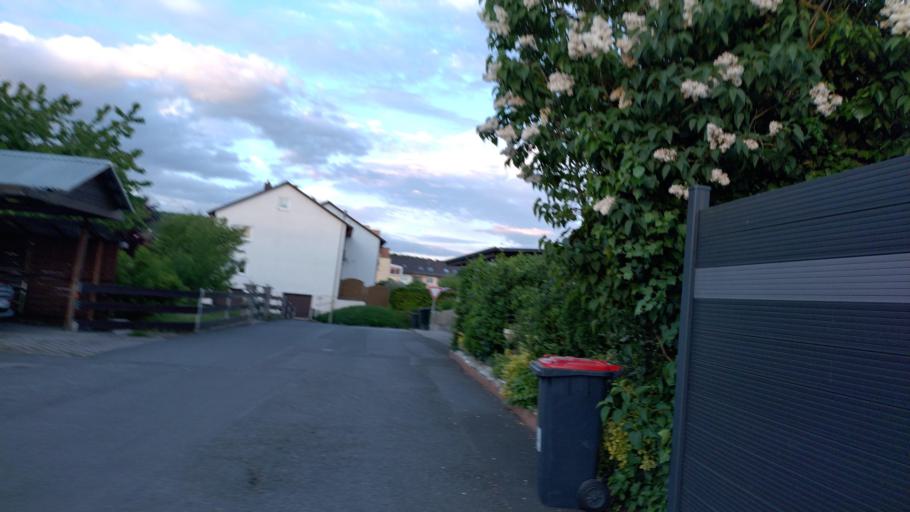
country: DE
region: Bavaria
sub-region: Upper Franconia
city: Bindlach
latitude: 49.9790
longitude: 11.6150
